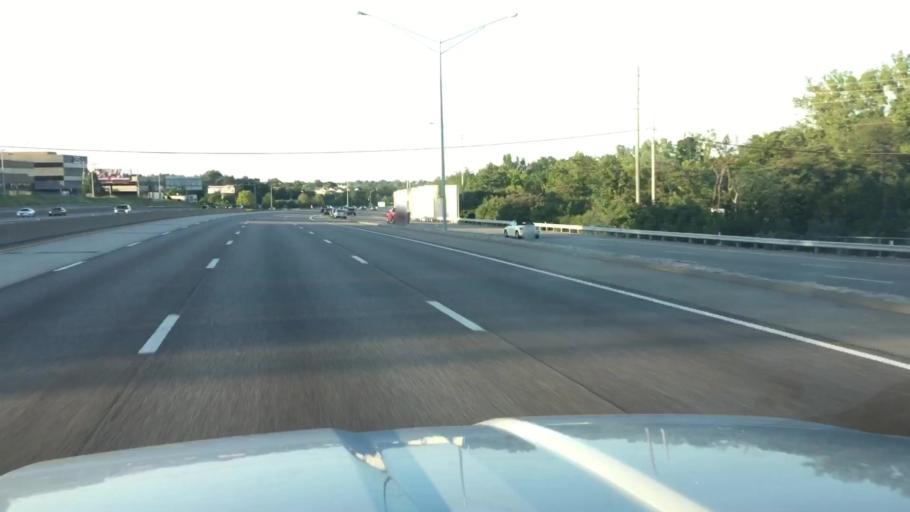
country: US
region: Missouri
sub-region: Saint Louis County
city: Green Park
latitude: 38.5137
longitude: -90.3353
